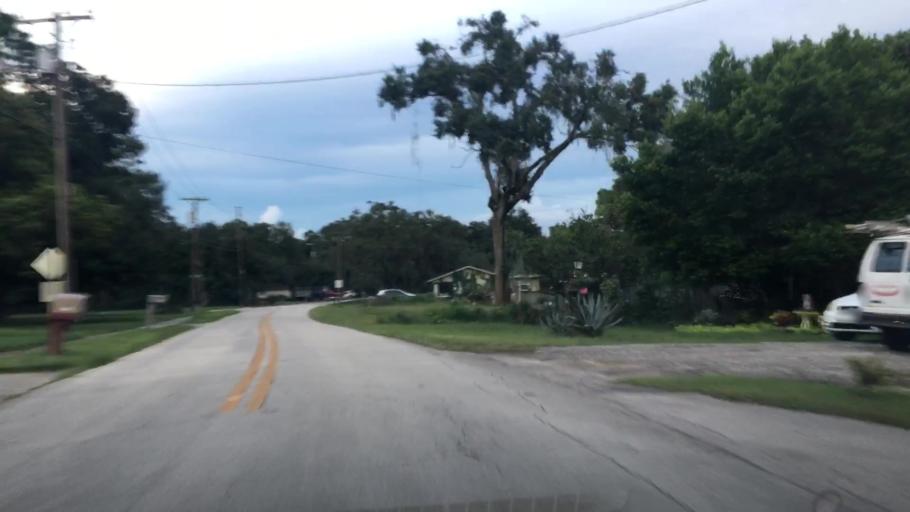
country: US
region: Florida
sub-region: Volusia County
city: DeBary
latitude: 28.8789
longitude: -81.3038
